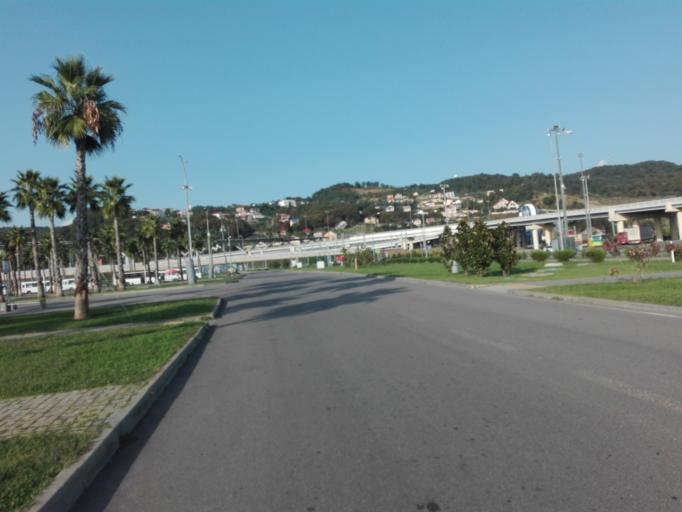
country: RU
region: Krasnodarskiy
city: Adler
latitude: 43.4092
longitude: 39.9743
